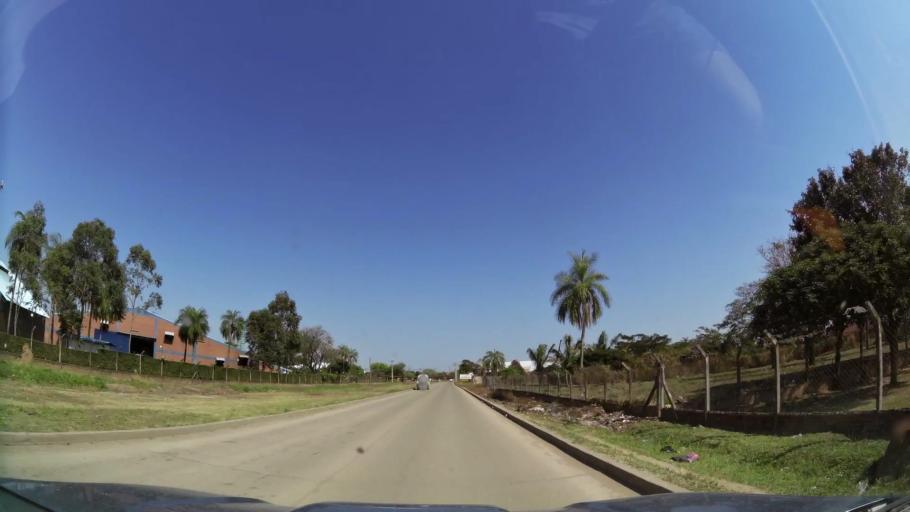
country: BO
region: Santa Cruz
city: Santa Cruz de la Sierra
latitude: -17.7560
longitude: -63.1204
